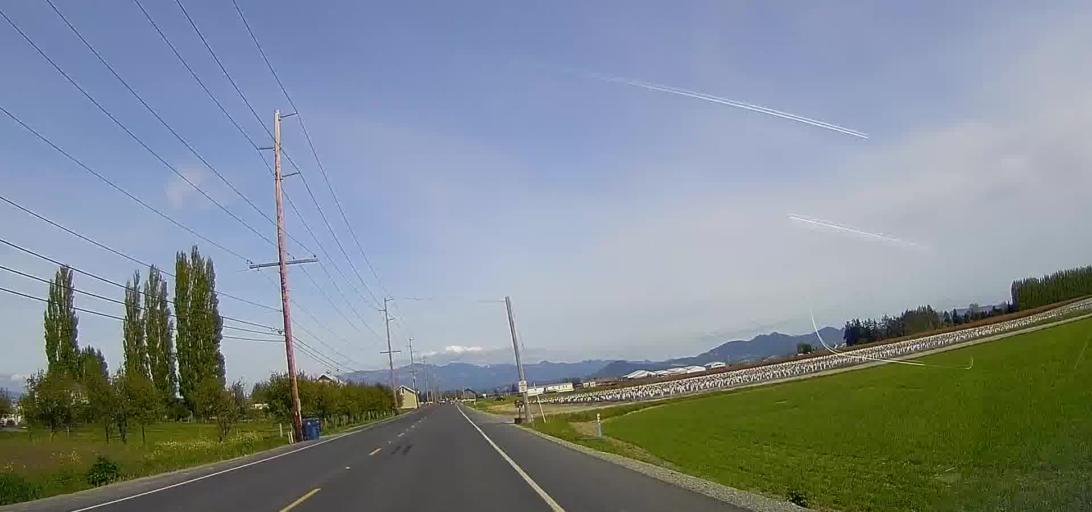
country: US
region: Washington
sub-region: Skagit County
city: Mount Vernon
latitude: 48.4210
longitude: -122.4547
